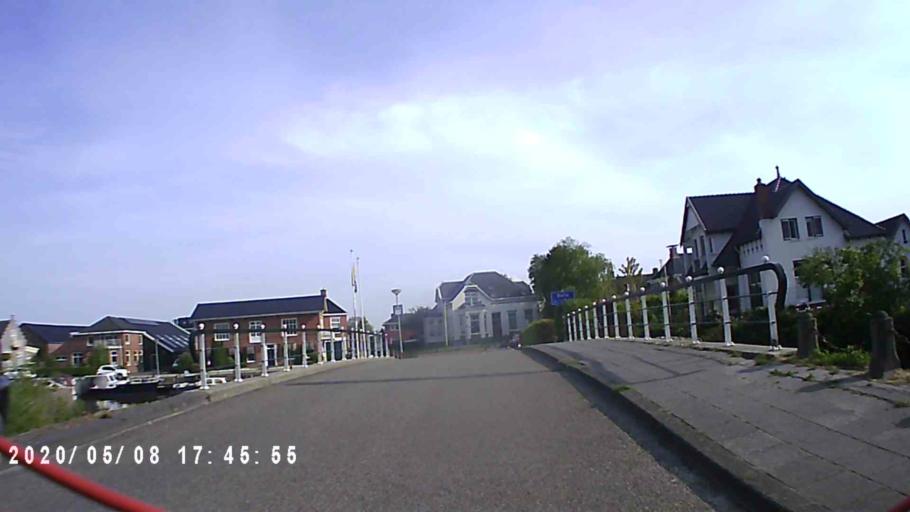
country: NL
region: Groningen
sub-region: Gemeente Winsum
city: Winsum
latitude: 53.3647
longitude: 6.5159
